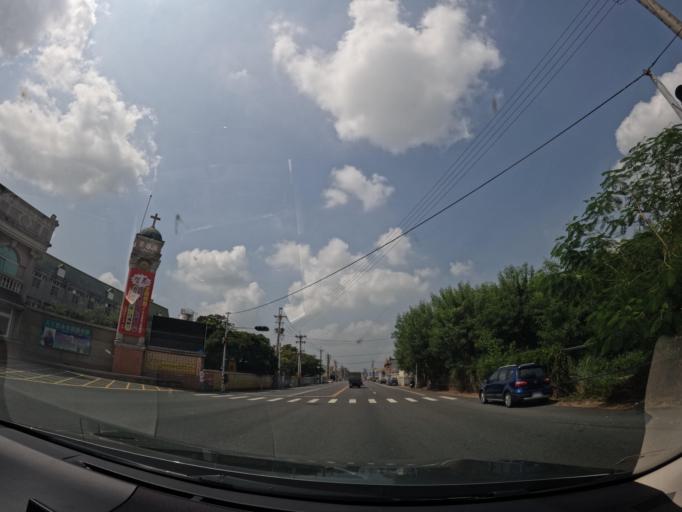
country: TW
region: Taiwan
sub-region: Yunlin
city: Douliu
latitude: 23.6800
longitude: 120.3997
